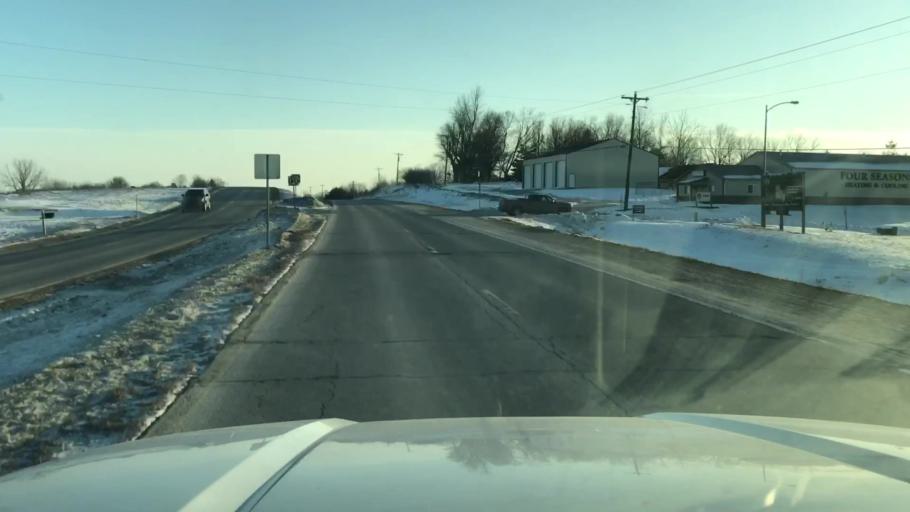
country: US
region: Missouri
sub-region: Andrew County
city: Country Club Village
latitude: 39.8799
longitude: -94.8091
